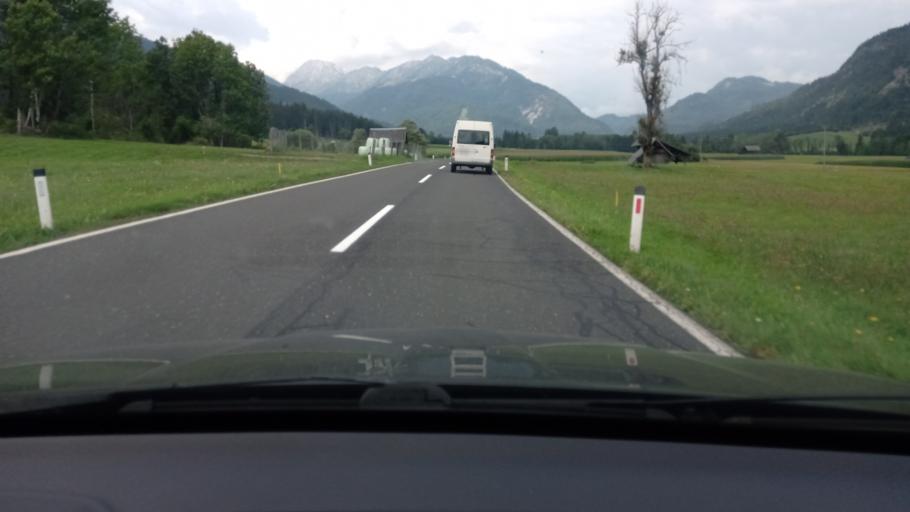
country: AT
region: Carinthia
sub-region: Politischer Bezirk Hermagor
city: Hermagor
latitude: 46.6681
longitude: 13.2950
